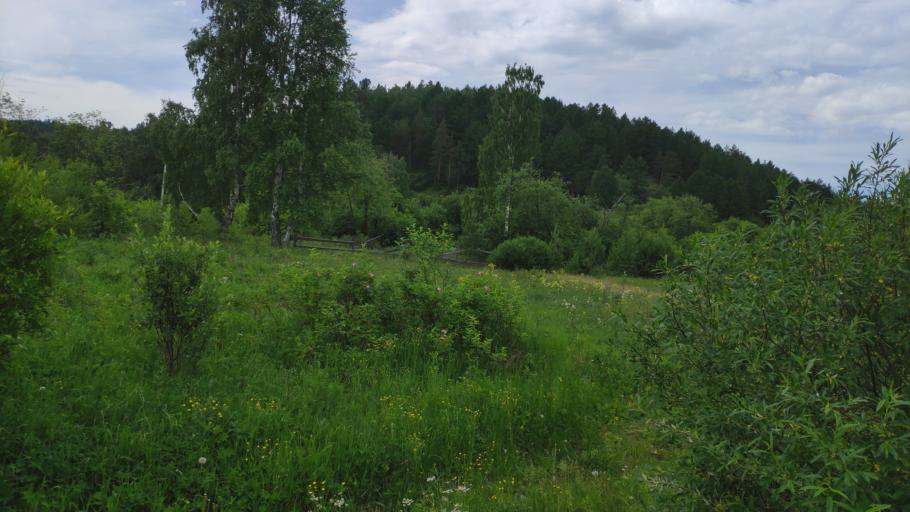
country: RU
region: Bashkortostan
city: Abzakovo
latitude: 53.8164
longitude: 58.6359
